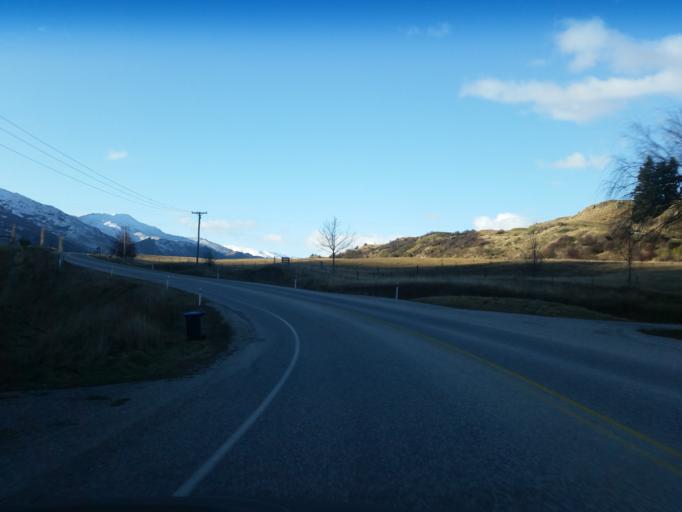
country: NZ
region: Otago
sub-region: Queenstown-Lakes District
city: Queenstown
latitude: -44.9704
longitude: 168.7018
